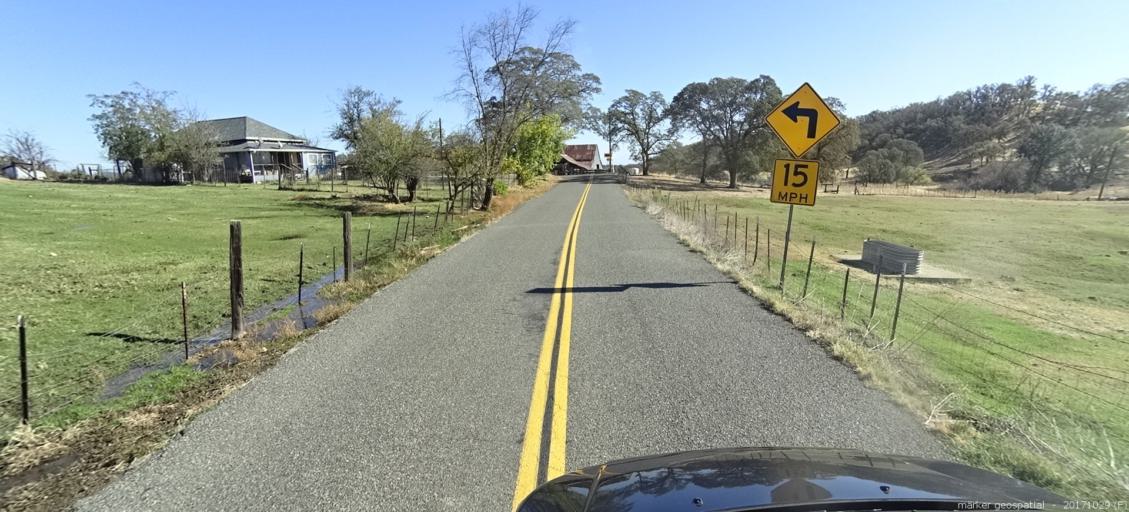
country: US
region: California
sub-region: Shasta County
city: Shasta
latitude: 40.4507
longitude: -122.6365
